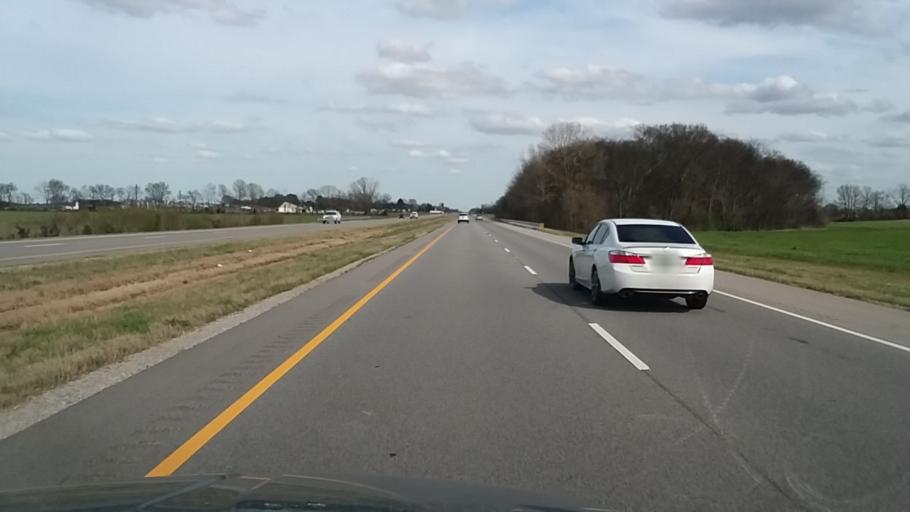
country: US
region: Alabama
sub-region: Colbert County
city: Muscle Shoals
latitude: 34.6849
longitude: -87.5773
